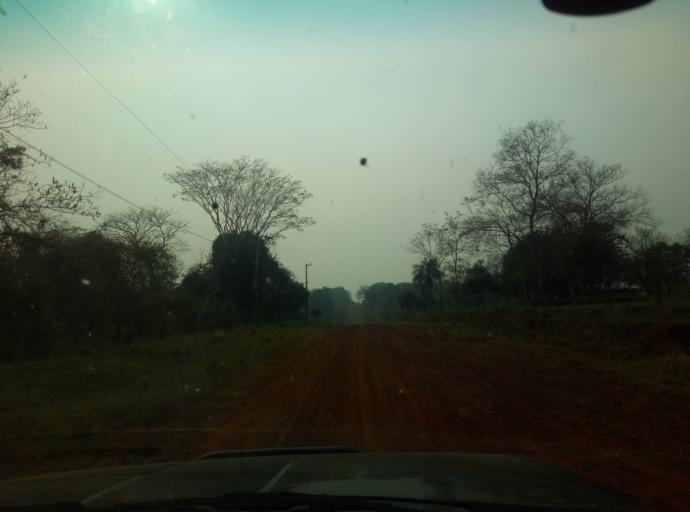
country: PY
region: Caaguazu
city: Carayao
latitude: -25.2038
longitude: -56.2335
